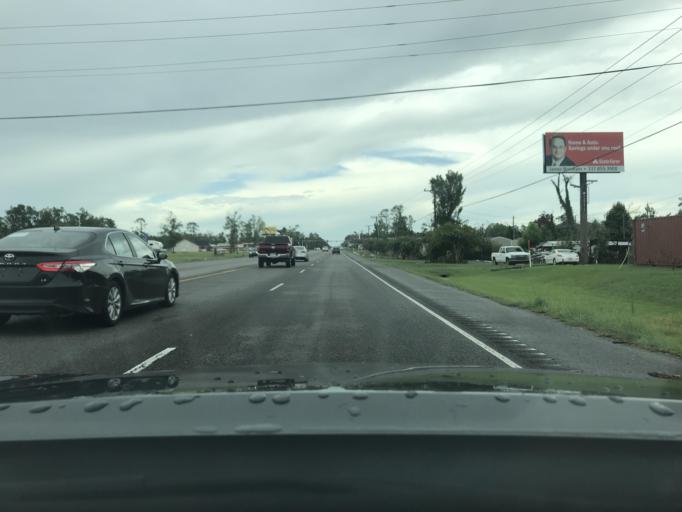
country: US
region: Louisiana
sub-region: Calcasieu Parish
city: Moss Bluff
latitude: 30.3007
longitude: -93.2373
